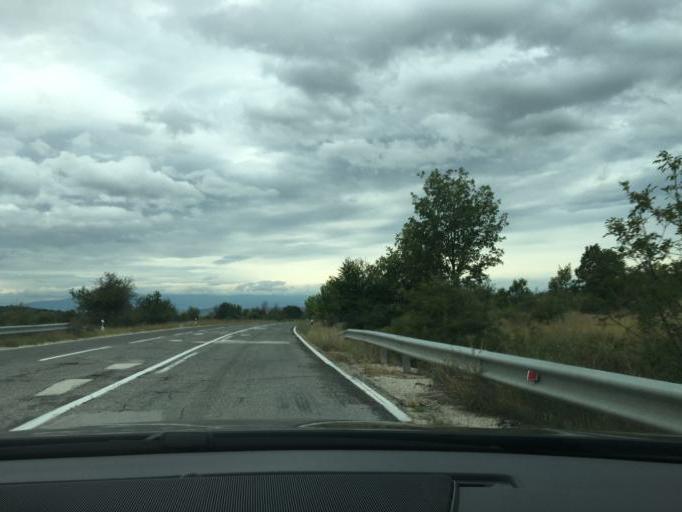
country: MK
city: Klechovce
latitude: 42.1493
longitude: 21.9673
